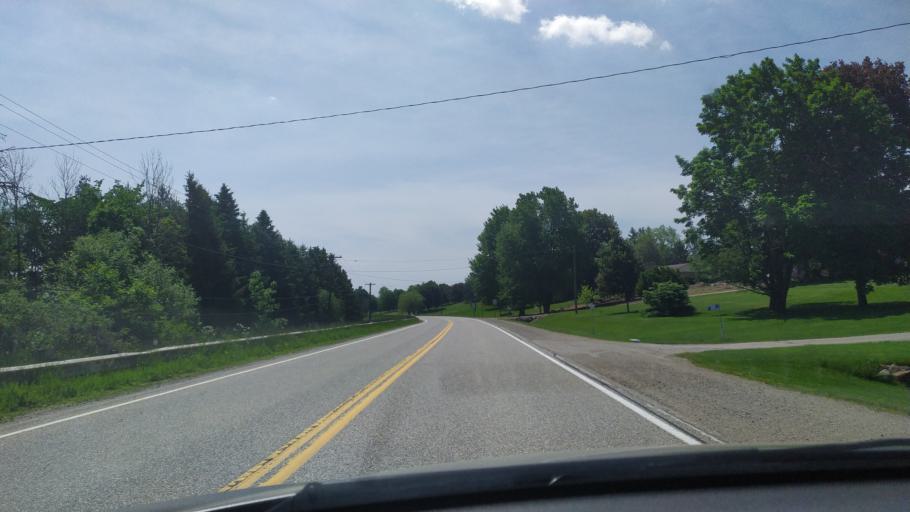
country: CA
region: Ontario
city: Dorchester
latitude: 43.0723
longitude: -81.0065
